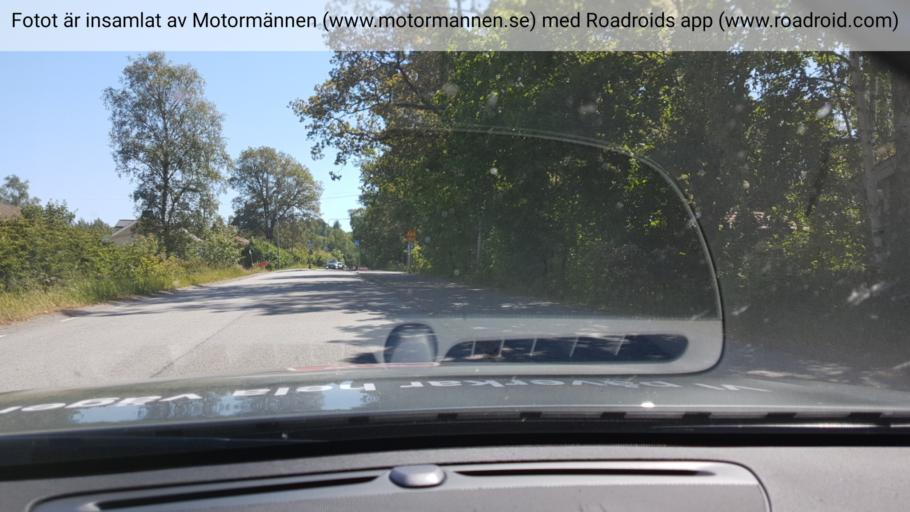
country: SE
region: Stockholm
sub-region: Huddinge Kommun
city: Huddinge
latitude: 59.2313
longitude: 17.9982
